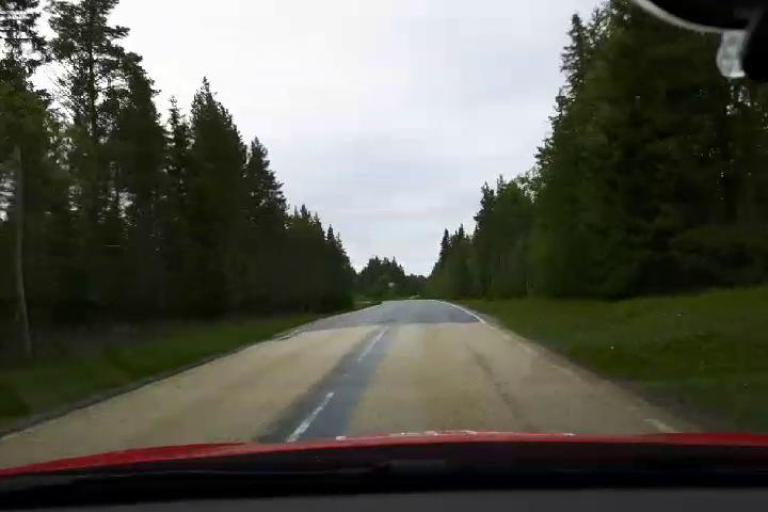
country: SE
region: Jaemtland
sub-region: Bergs Kommun
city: Hoverberg
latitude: 62.9013
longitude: 14.3434
